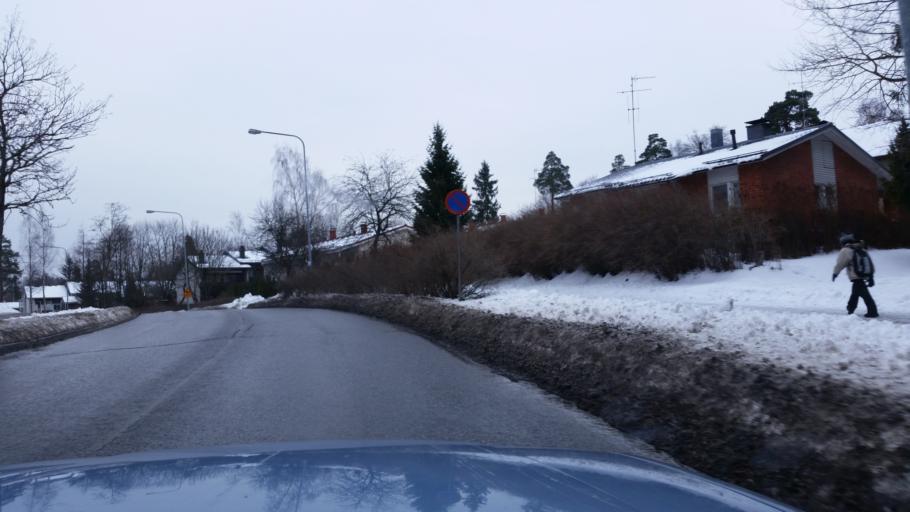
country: FI
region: Uusimaa
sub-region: Helsinki
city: Vantaa
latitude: 60.2701
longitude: 25.0545
